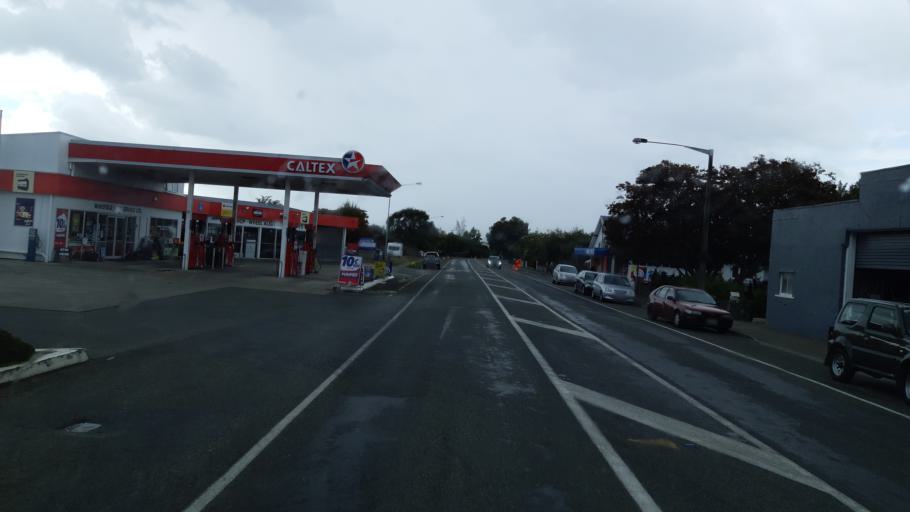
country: NZ
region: Tasman
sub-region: Tasman District
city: Wakefield
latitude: -41.4045
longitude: 173.0450
